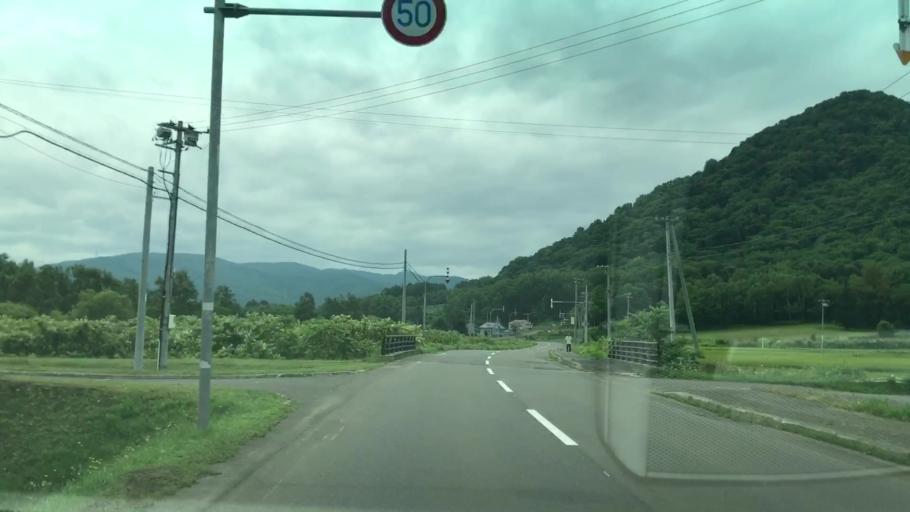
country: JP
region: Hokkaido
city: Yoichi
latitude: 43.0754
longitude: 140.8165
